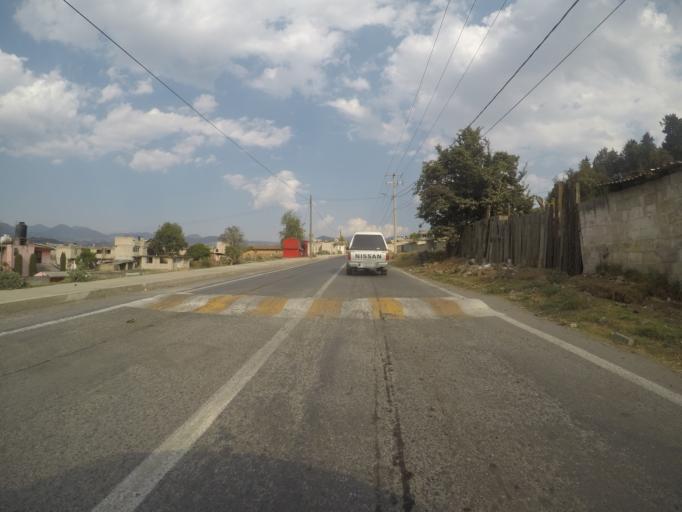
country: MX
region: Mexico
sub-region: Xalatlaco
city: Techichili
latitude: 19.1751
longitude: -99.4241
